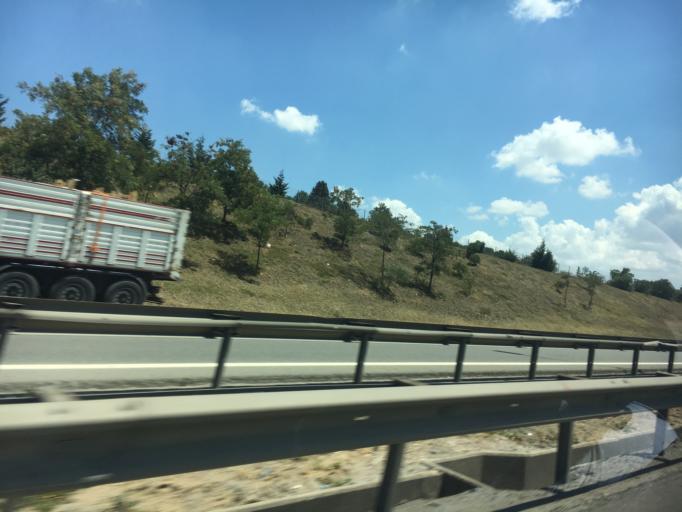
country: TR
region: Kocaeli
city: Balcik
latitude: 40.8915
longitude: 29.3716
